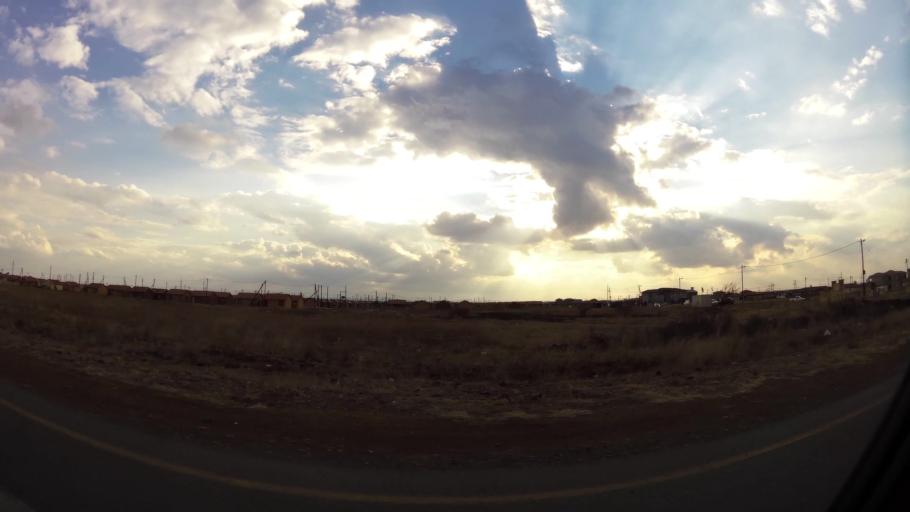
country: ZA
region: Gauteng
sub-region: Sedibeng District Municipality
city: Vanderbijlpark
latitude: -26.6147
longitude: 27.8138
